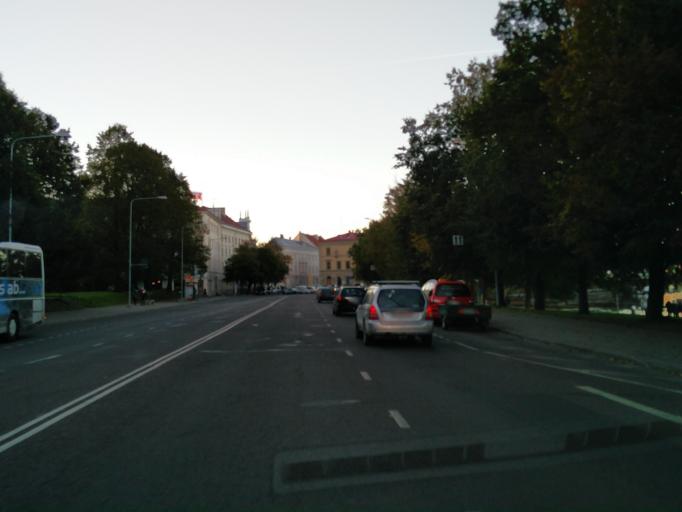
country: EE
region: Tartu
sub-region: Tartu linn
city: Tartu
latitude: 58.3792
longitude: 26.7270
